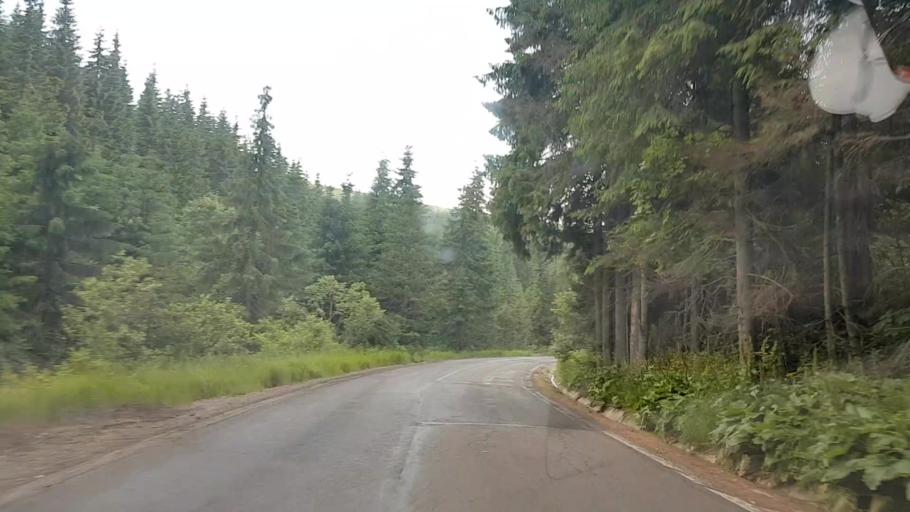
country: RO
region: Harghita
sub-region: Comuna Varsag
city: Varsag
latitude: 46.6447
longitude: 25.2862
